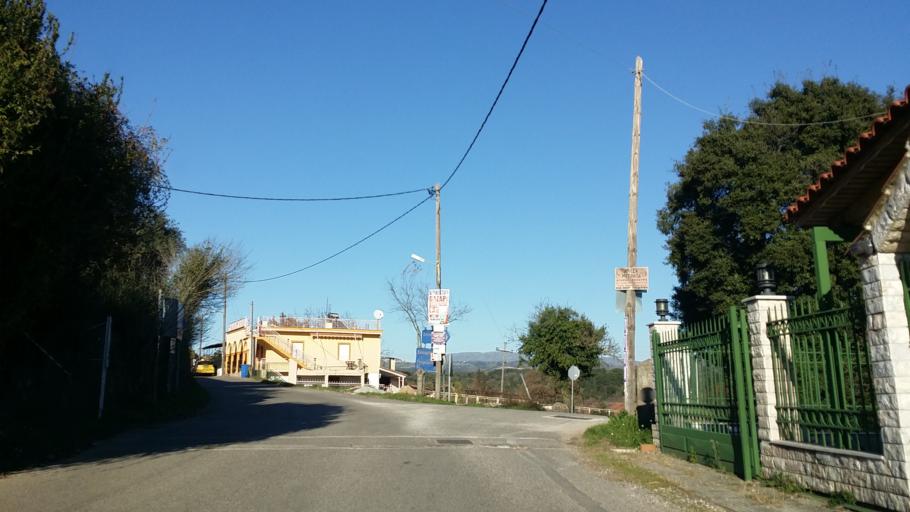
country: GR
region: West Greece
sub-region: Nomos Aitolias kai Akarnanias
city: Fitiai
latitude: 38.6305
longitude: 21.1523
